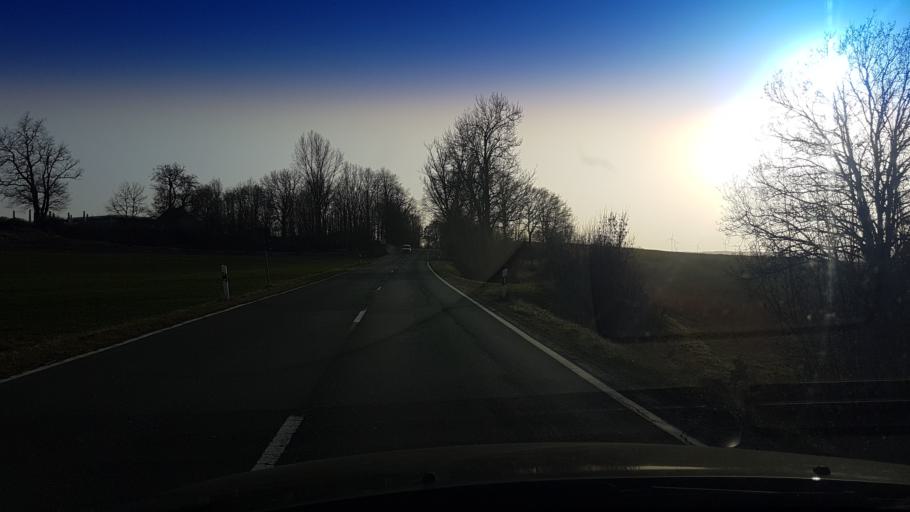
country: DE
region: Bavaria
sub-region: Upper Franconia
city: Pommersfelden
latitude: 49.7596
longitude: 10.8189
